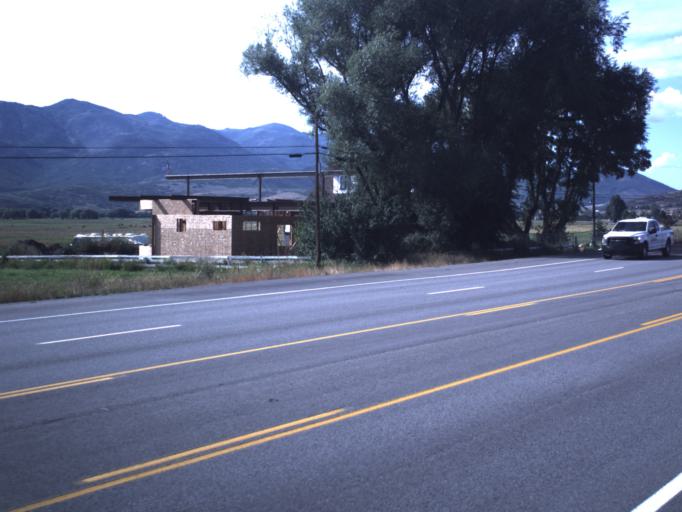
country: US
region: Utah
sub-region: Wasatch County
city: Heber
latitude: 40.5278
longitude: -111.4095
